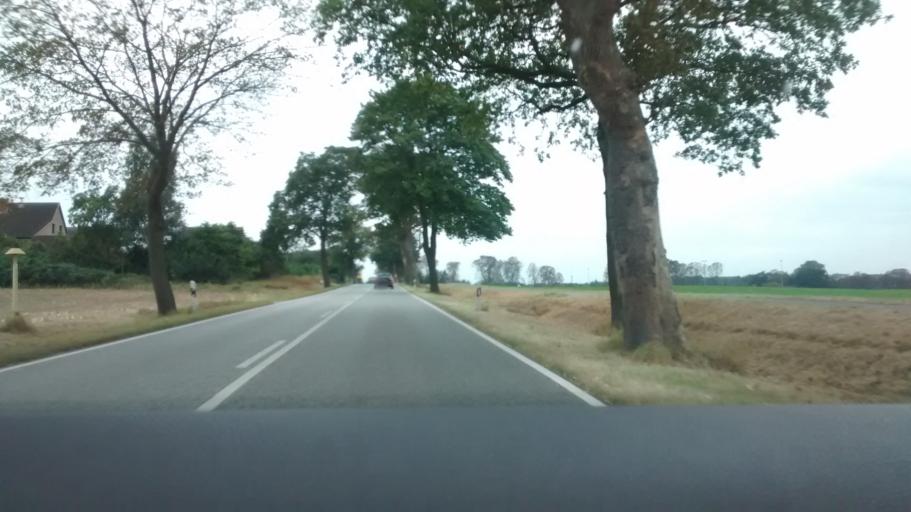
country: DE
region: Mecklenburg-Vorpommern
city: Mecklenburg
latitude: 53.8192
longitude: 11.4500
